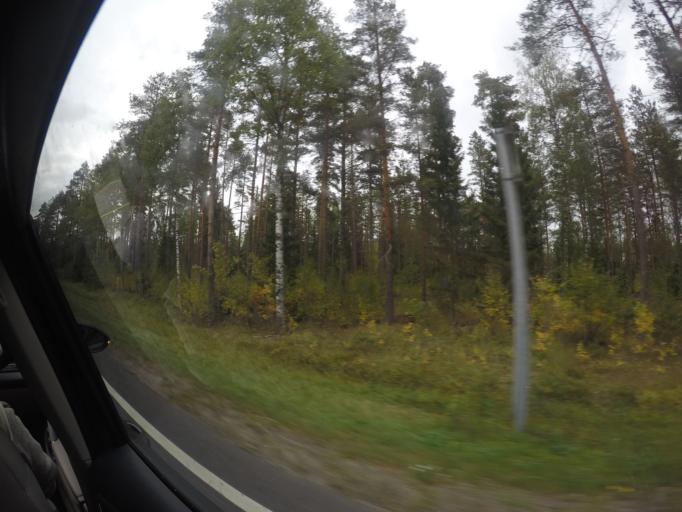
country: FI
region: Pirkanmaa
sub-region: Ylae-Pirkanmaa
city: Juupajoki
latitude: 61.8351
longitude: 24.2796
